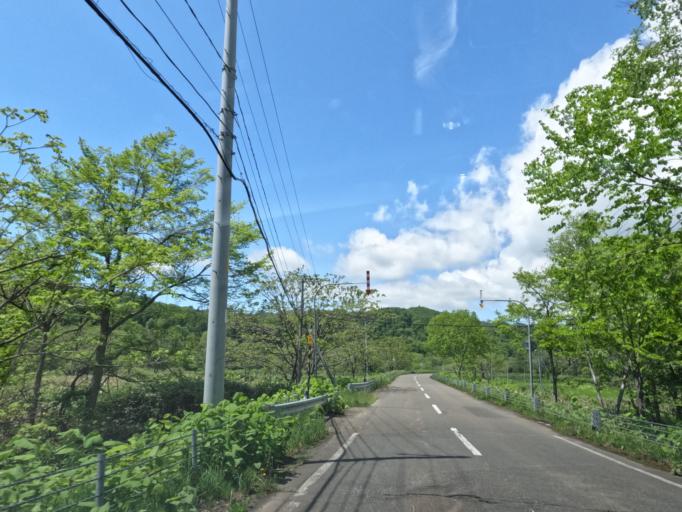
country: JP
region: Hokkaido
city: Tobetsu
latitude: 43.4272
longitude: 141.5801
